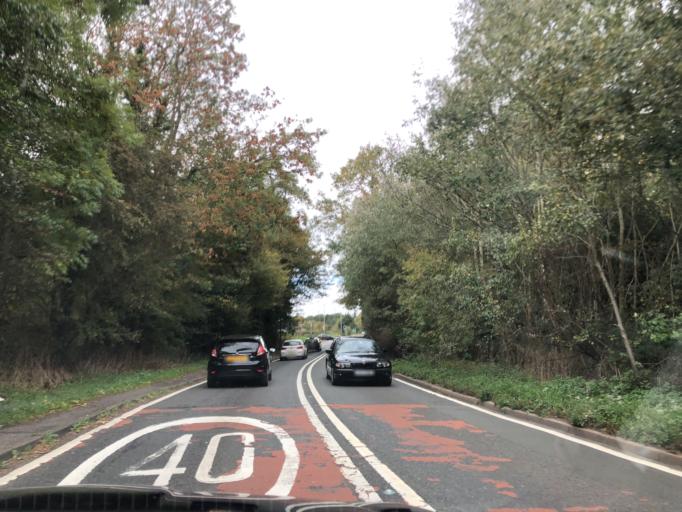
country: GB
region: England
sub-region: Warwickshire
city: Kenilworth
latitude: 52.3260
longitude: -1.5568
